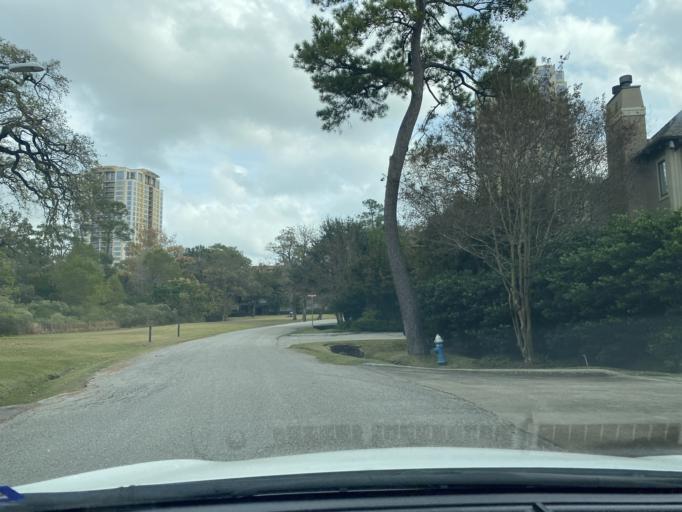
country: US
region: Texas
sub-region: Harris County
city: Hunters Creek Village
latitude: 29.7567
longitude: -95.4609
